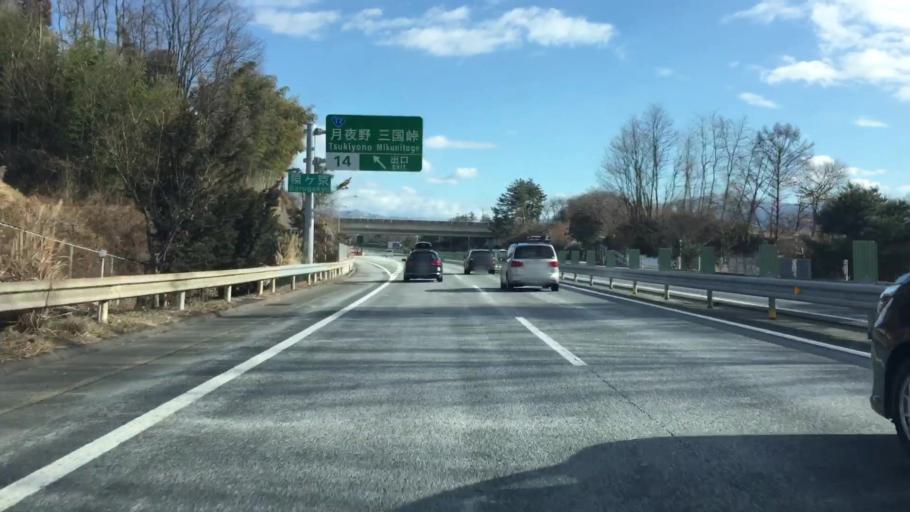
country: JP
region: Gunma
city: Numata
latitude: 36.6775
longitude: 139.0145
